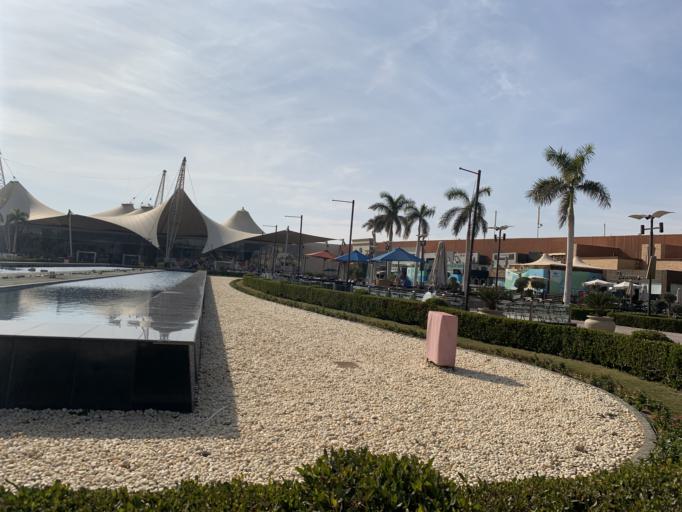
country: EG
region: Al Jizah
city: Awsim
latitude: 30.0066
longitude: 30.9738
